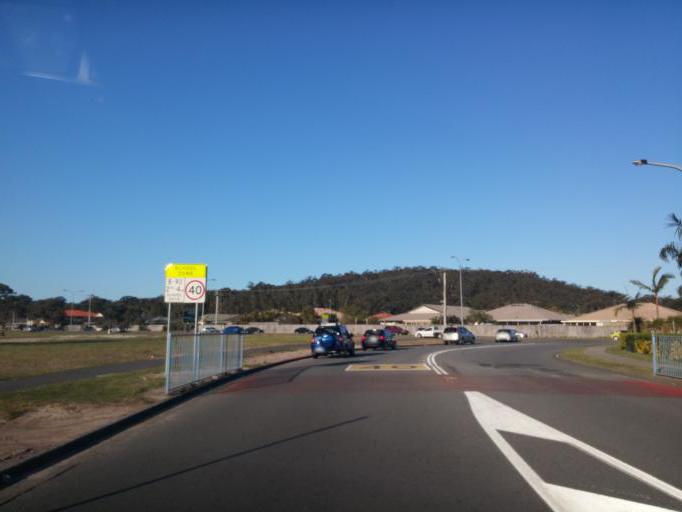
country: AU
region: New South Wales
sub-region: Port Stephens Shire
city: Corlette
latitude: -32.7358
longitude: 152.1085
